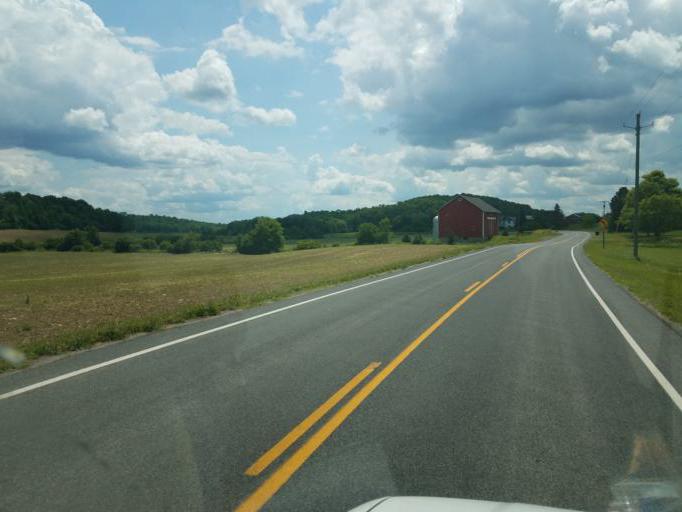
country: US
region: New York
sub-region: Wayne County
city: Clyde
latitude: 43.0636
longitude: -76.8576
